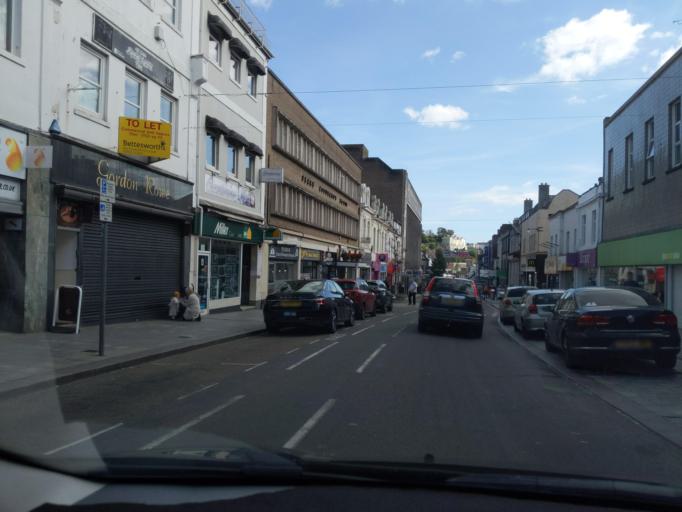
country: GB
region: England
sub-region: Borough of Torbay
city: Torquay
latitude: 50.4680
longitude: -3.5316
